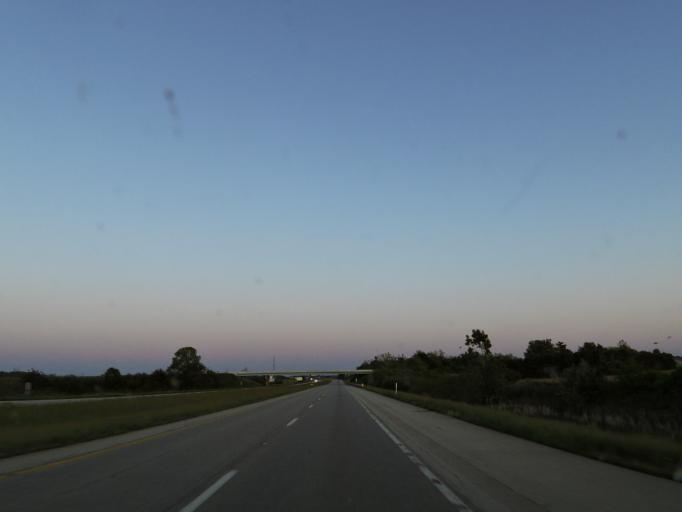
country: US
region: Indiana
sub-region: Montgomery County
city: Crawfordsville
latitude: 40.0303
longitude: -86.7916
